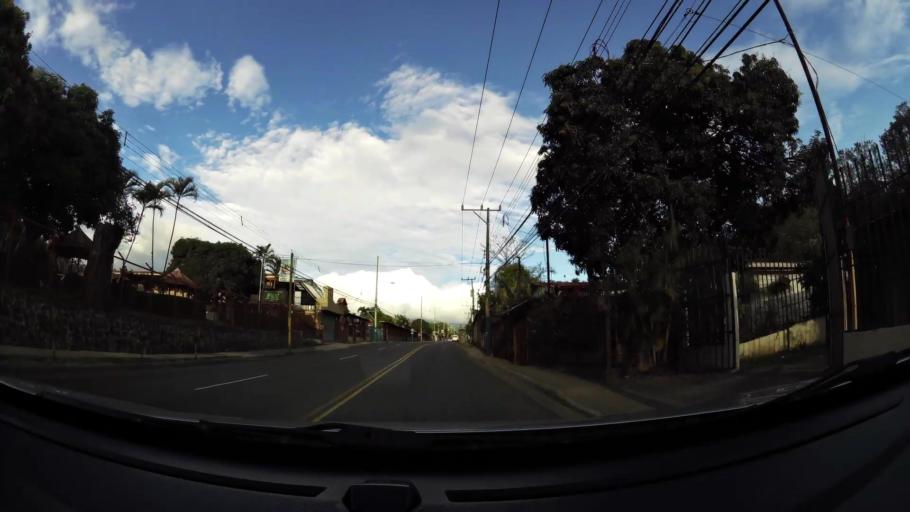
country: CR
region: Heredia
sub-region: Canton de Belen
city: San Antonio
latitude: 10.0048
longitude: -84.1819
